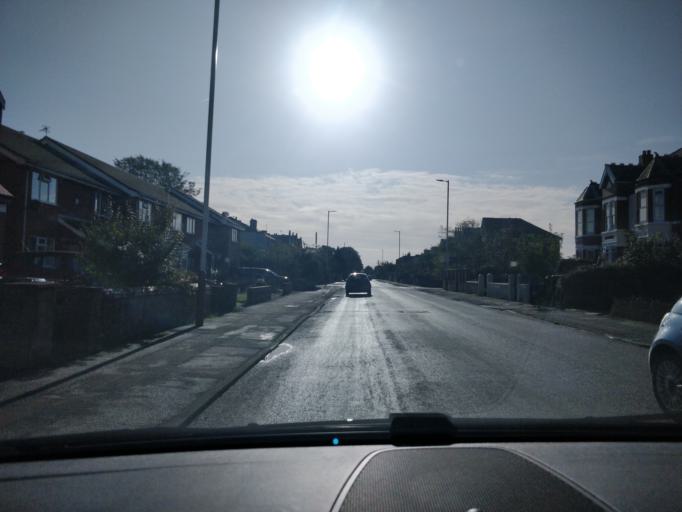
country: GB
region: England
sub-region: Sefton
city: Southport
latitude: 53.6365
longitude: -3.0024
